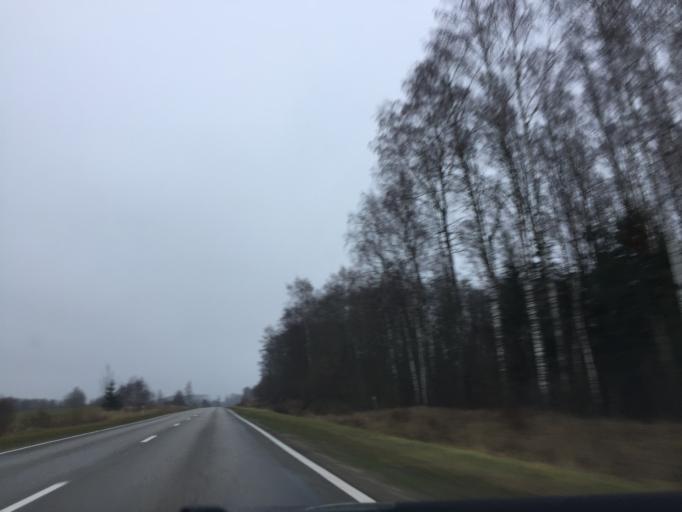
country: LV
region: Pargaujas
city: Stalbe
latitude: 57.4156
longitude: 25.1323
